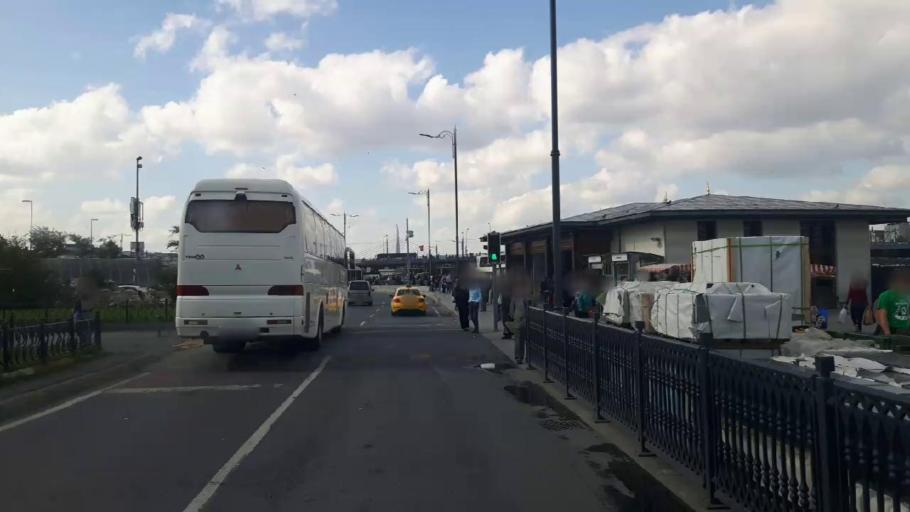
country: TR
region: Istanbul
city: Eminoenue
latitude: 41.0175
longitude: 28.9743
